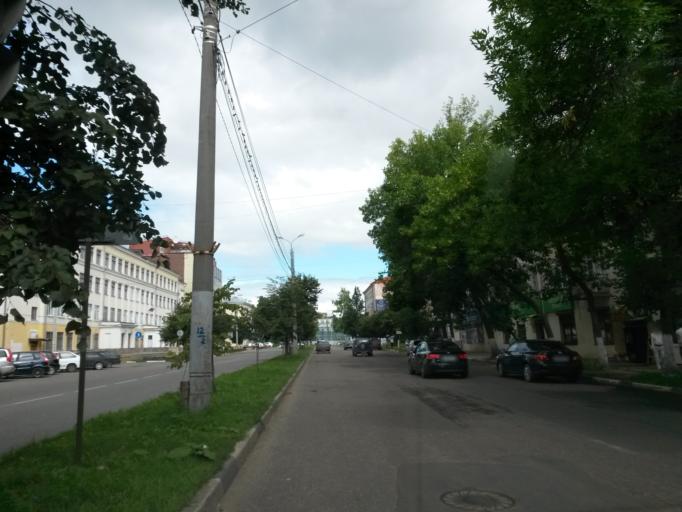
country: RU
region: Jaroslavl
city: Yaroslavl
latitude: 57.6327
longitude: 39.8708
